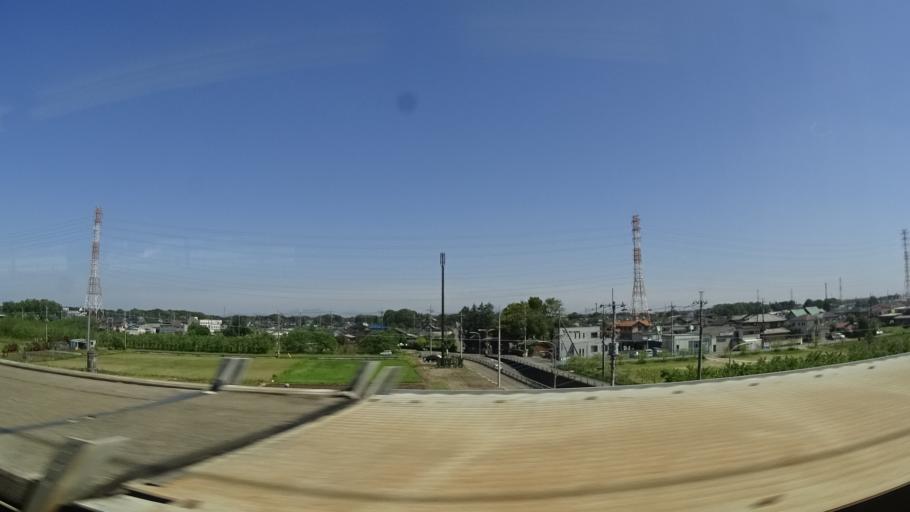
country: JP
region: Tochigi
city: Oyama
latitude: 36.3372
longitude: 139.8204
